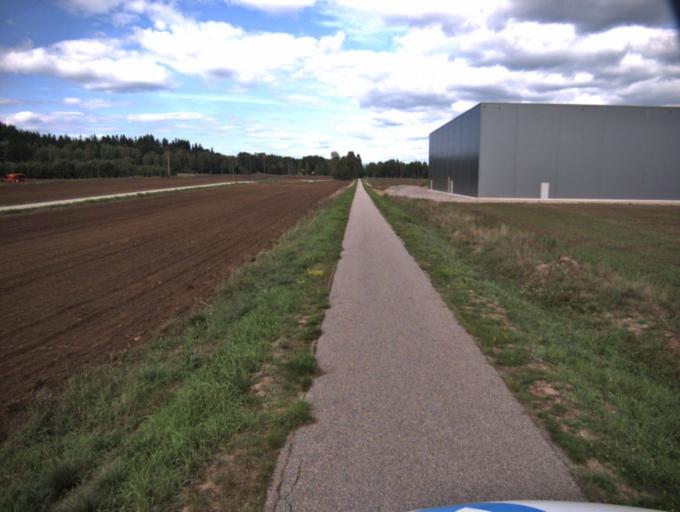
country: SE
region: Vaestra Goetaland
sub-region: Ulricehamns Kommun
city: Ulricehamn
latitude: 57.8392
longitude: 13.4208
